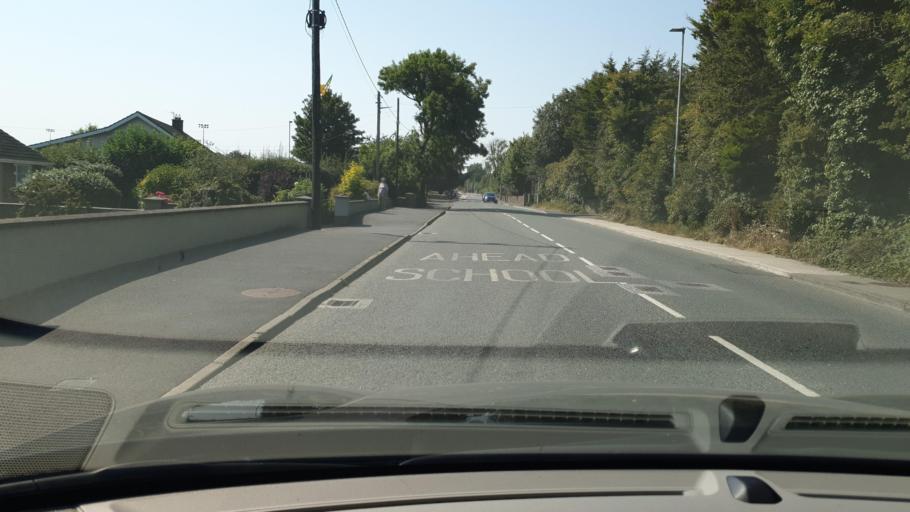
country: IE
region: Leinster
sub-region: An Mhi
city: Dunshaughlin
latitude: 53.5154
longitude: -6.5477
